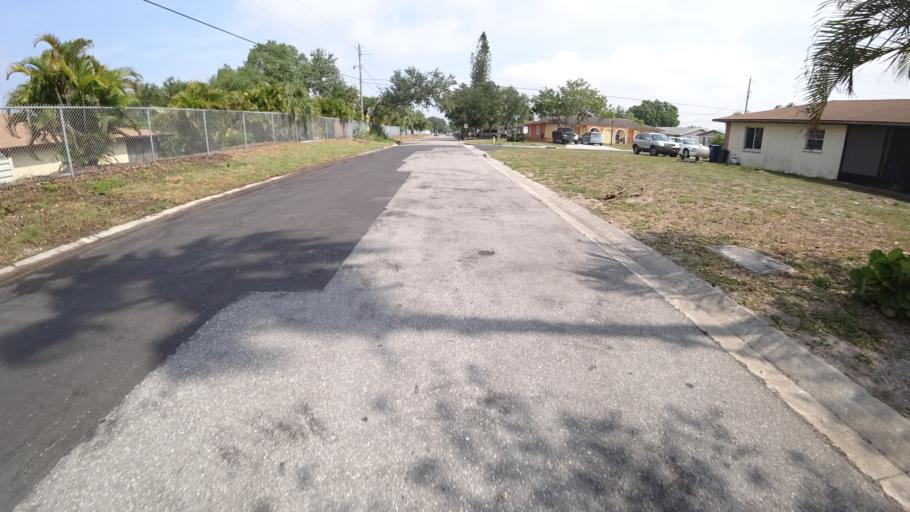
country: US
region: Florida
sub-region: Manatee County
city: West Bradenton
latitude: 27.4642
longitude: -82.6246
